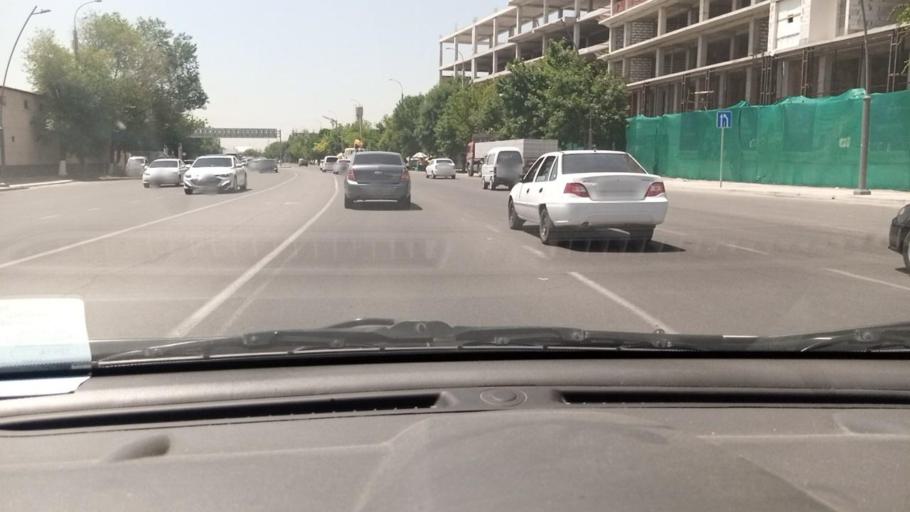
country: UZ
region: Toshkent Shahri
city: Tashkent
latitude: 41.2651
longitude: 69.2376
